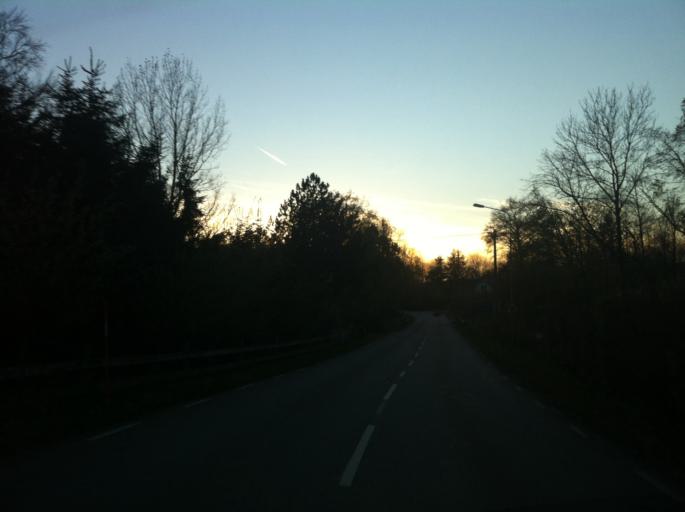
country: SE
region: Skane
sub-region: Eslovs Kommun
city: Eslov
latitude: 55.8781
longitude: 13.2581
